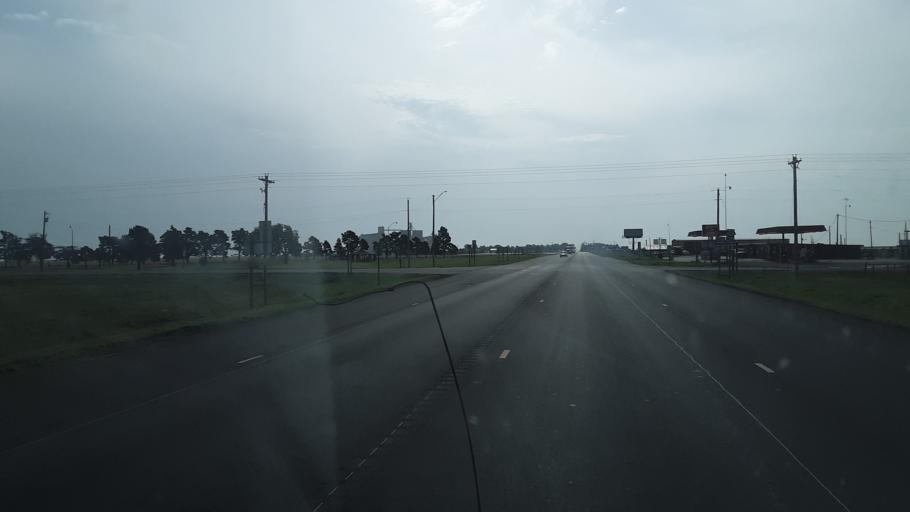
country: US
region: Kansas
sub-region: Ford County
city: Dodge City
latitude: 37.7789
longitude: -99.9069
